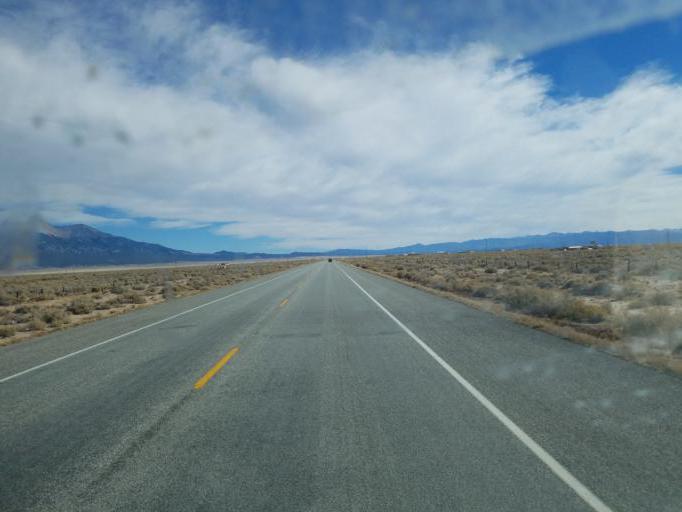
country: US
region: Colorado
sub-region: Alamosa County
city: Alamosa East
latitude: 37.4750
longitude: -105.7048
